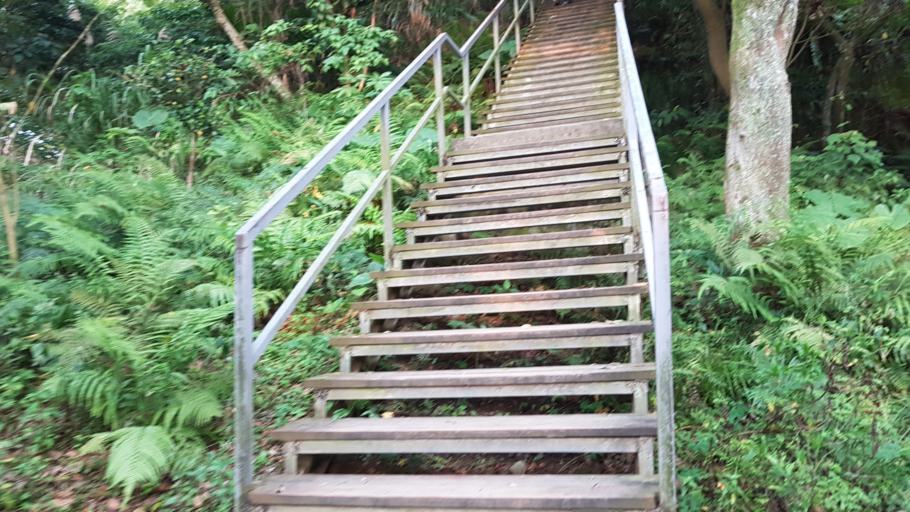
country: TW
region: Taipei
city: Taipei
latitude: 25.0168
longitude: 121.5526
